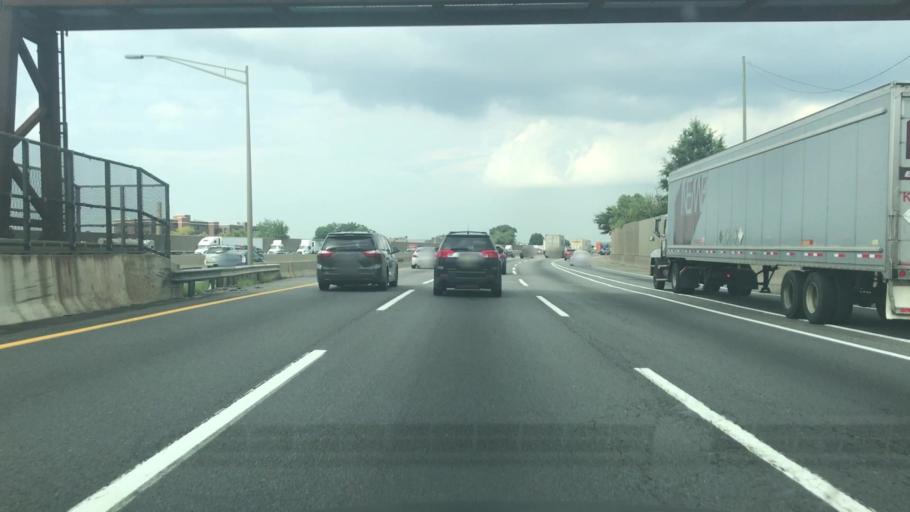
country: US
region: New Jersey
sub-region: Union County
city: Elizabeth
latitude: 40.6486
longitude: -74.2008
